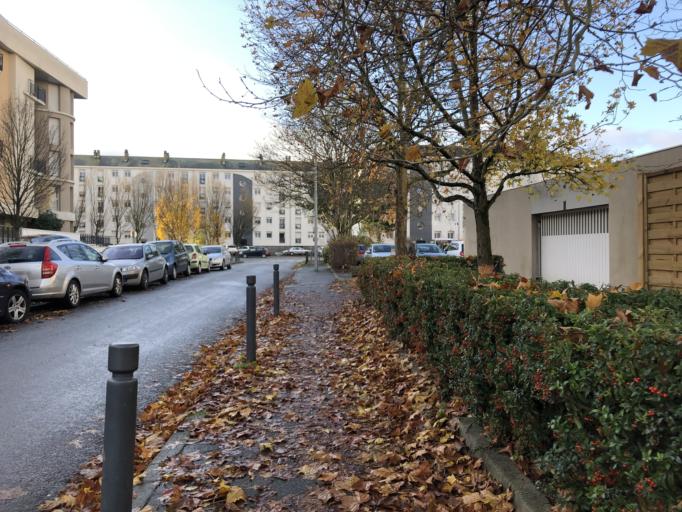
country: FR
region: Pays de la Loire
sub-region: Departement de Maine-et-Loire
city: Angers
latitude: 47.4686
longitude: -0.5366
